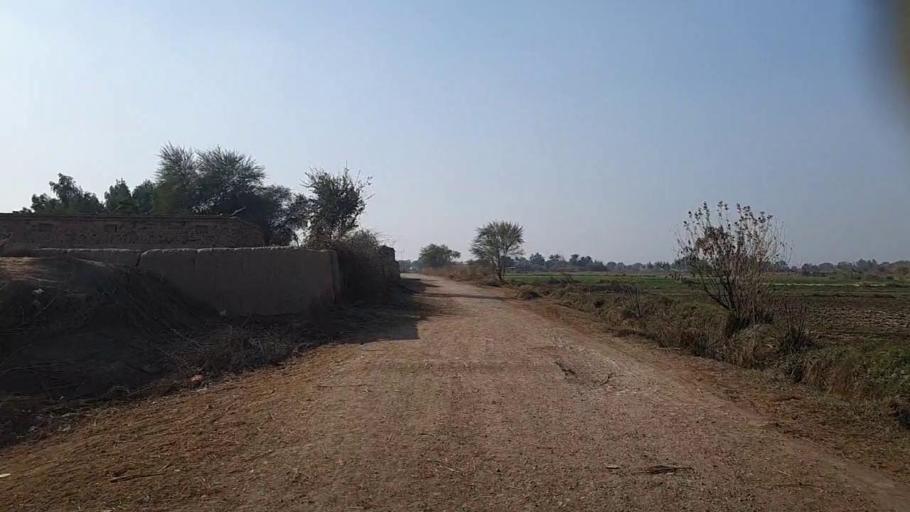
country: PK
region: Sindh
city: Mirpur Mathelo
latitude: 27.9027
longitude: 69.6215
